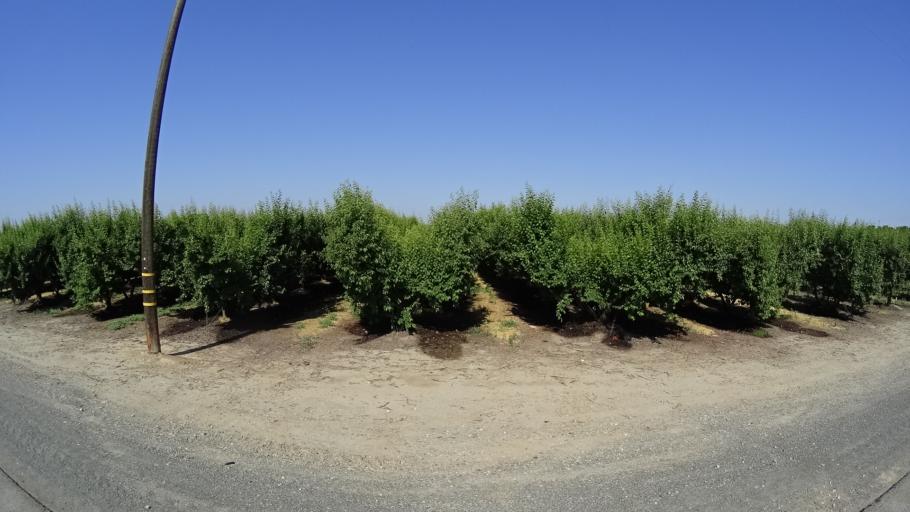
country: US
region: California
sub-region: Fresno County
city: Kingsburg
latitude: 36.4287
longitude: -119.5648
